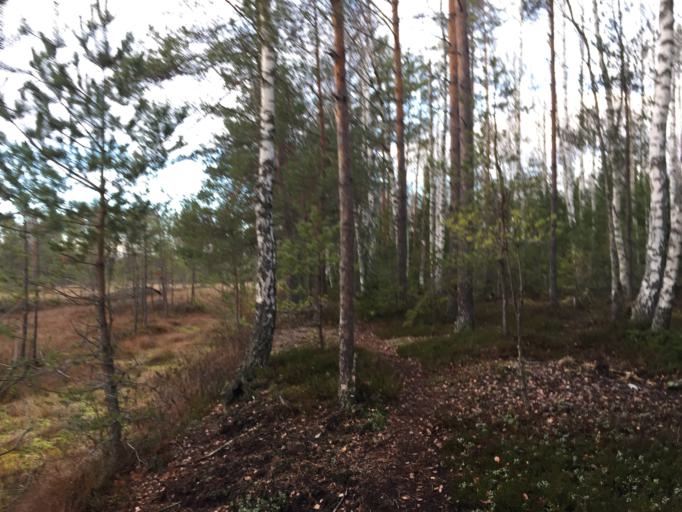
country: LV
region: Koceni
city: Koceni
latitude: 57.5368
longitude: 25.3757
